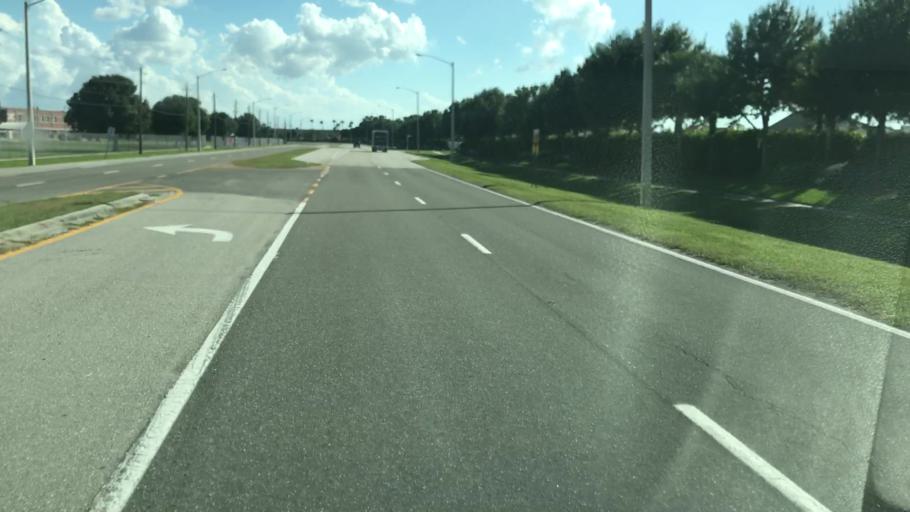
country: US
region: Florida
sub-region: Lee County
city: Fort Myers
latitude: 26.6018
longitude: -81.8183
